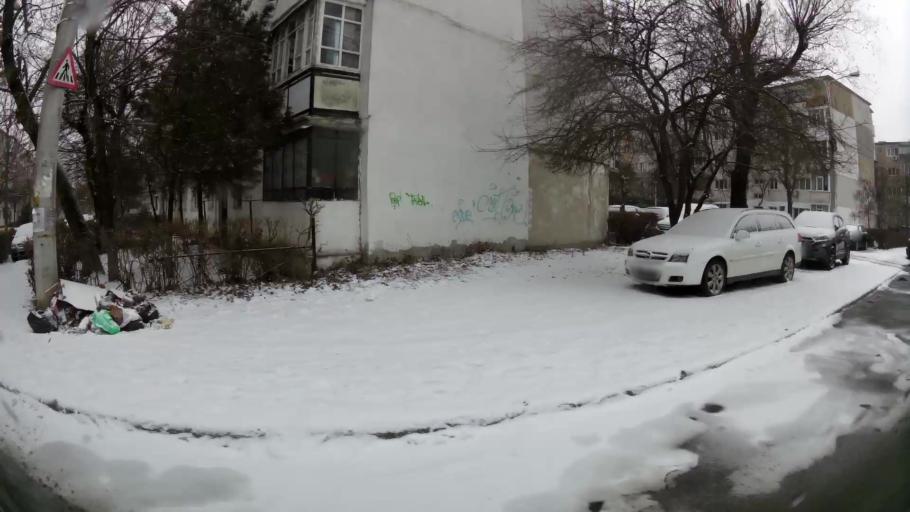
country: RO
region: Prahova
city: Ploiesti
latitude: 44.9337
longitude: 25.9961
